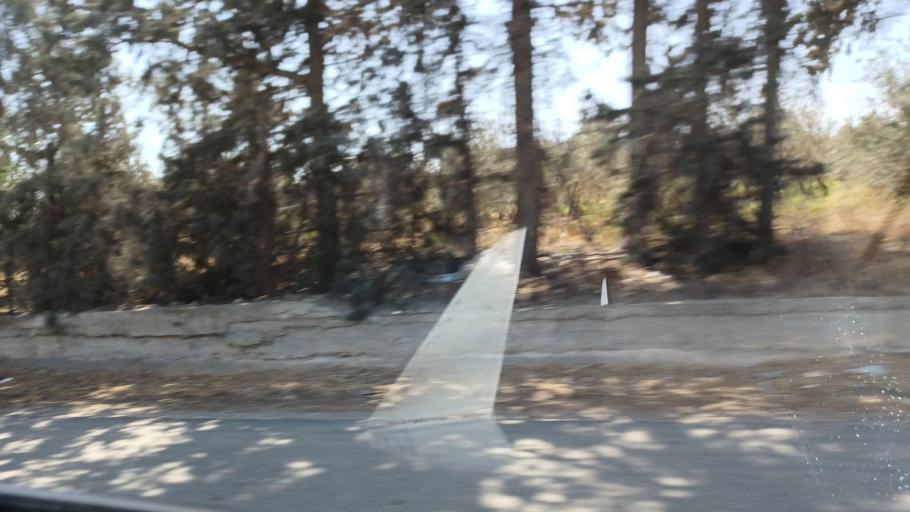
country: CY
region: Lefkosia
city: Akaki
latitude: 35.1351
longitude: 33.1167
